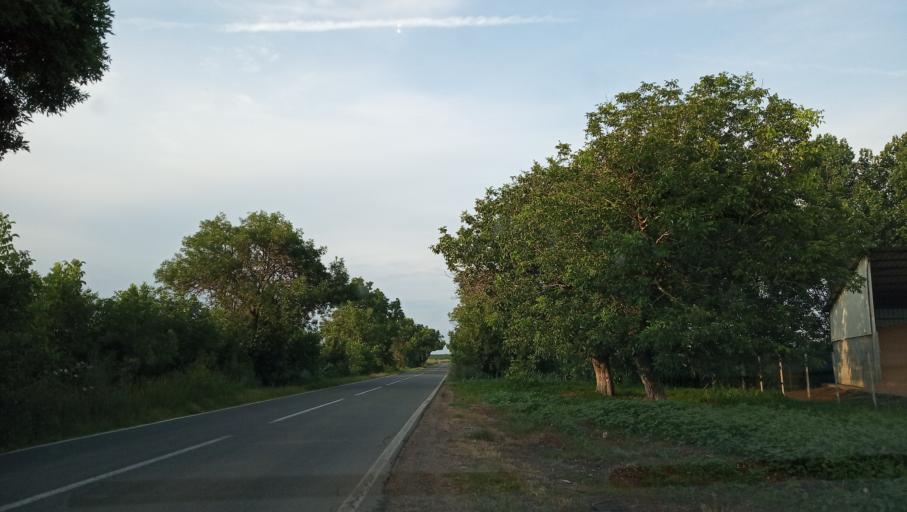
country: RO
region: Giurgiu
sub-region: Comuna Greaca
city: Greaca
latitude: 44.1236
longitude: 26.3795
